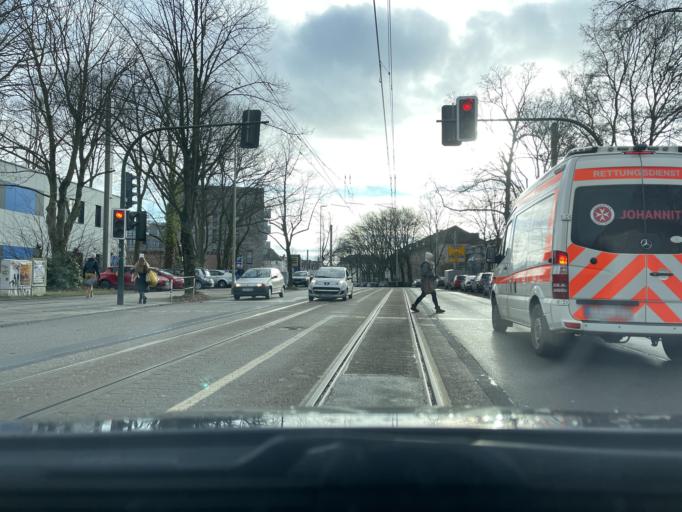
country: DE
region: North Rhine-Westphalia
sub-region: Regierungsbezirk Dusseldorf
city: Essen
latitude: 51.4397
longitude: 6.9885
